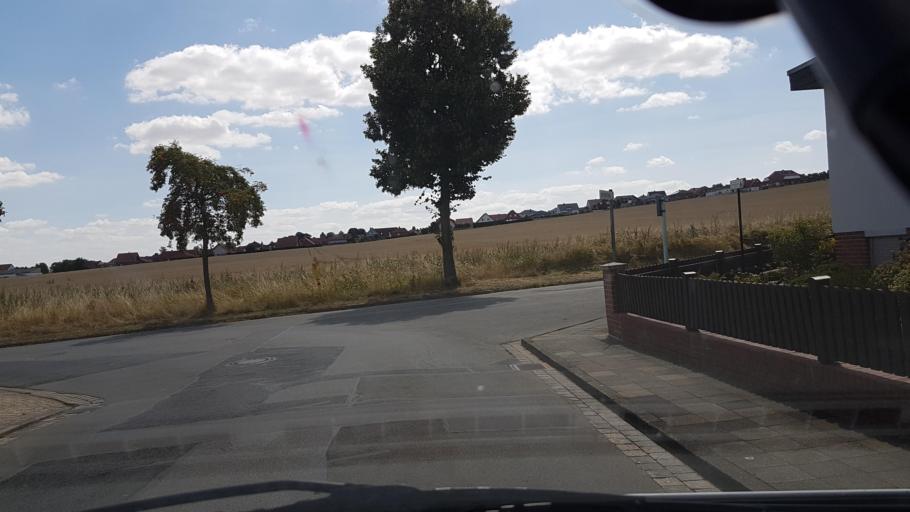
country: DE
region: Lower Saxony
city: Schoningen
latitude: 52.1541
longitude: 10.9609
